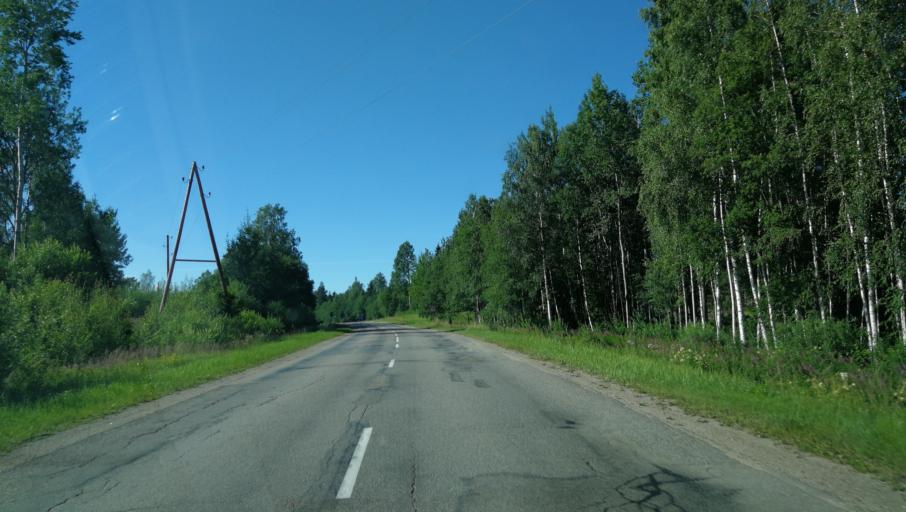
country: LV
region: Madonas Rajons
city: Madona
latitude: 56.9715
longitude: 26.0472
